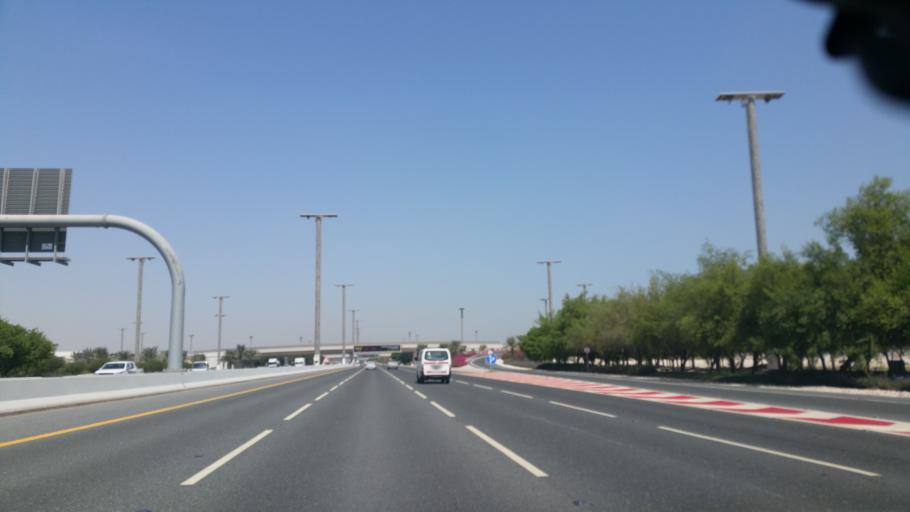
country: QA
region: Baladiyat ad Dawhah
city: Doha
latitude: 25.2539
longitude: 51.5859
